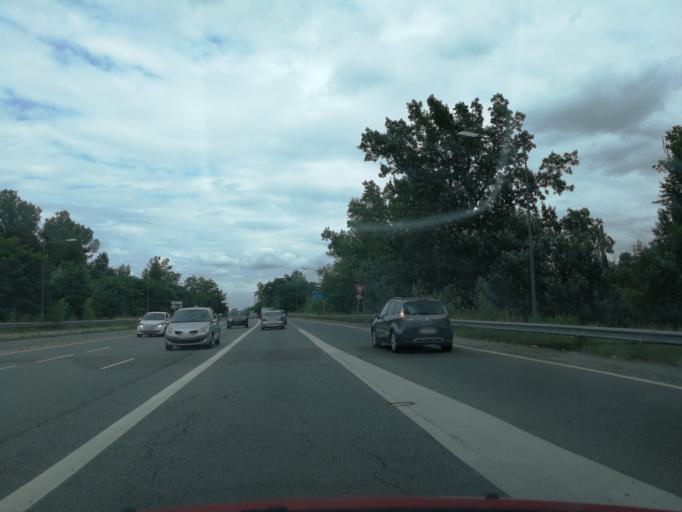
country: FR
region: Midi-Pyrenees
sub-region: Departement de la Haute-Garonne
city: Ramonville-Saint-Agne
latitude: 43.5546
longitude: 1.4784
